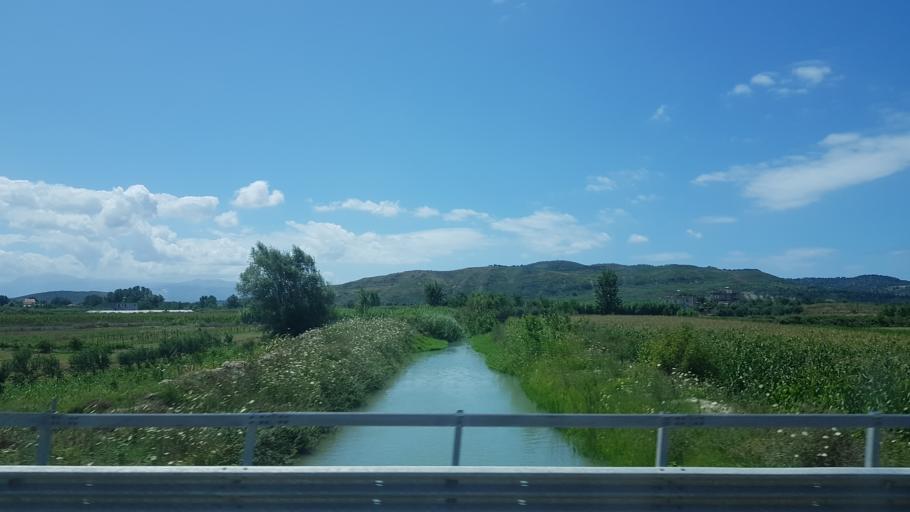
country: AL
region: Fier
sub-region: Rrethi i Fierit
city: Frakulla e Madhe
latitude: 40.6077
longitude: 19.5376
